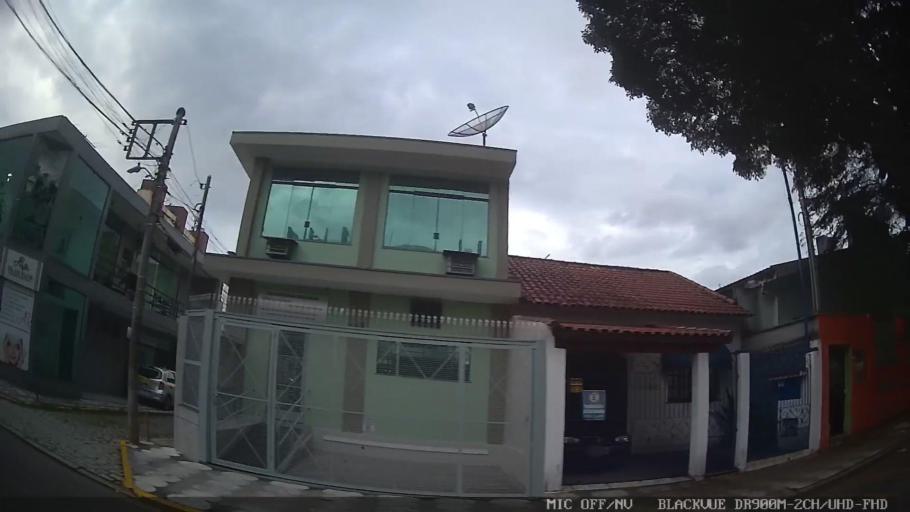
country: BR
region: Sao Paulo
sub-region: Mogi das Cruzes
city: Mogi das Cruzes
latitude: -23.5267
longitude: -46.1978
